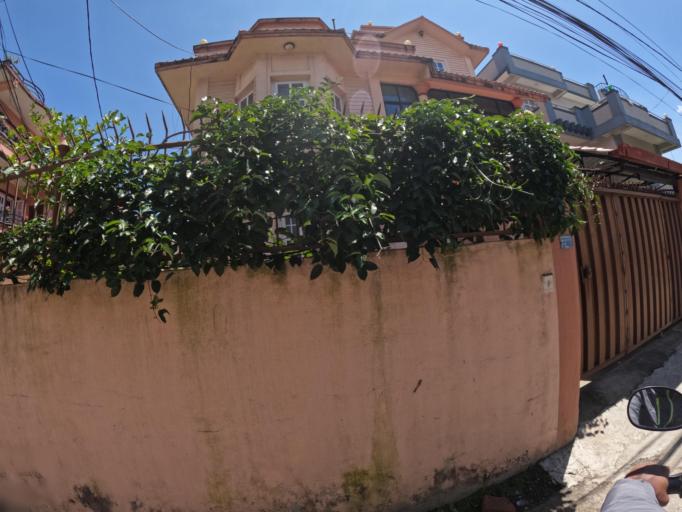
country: NP
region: Central Region
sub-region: Bagmati Zone
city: Kathmandu
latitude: 27.7500
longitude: 85.3265
